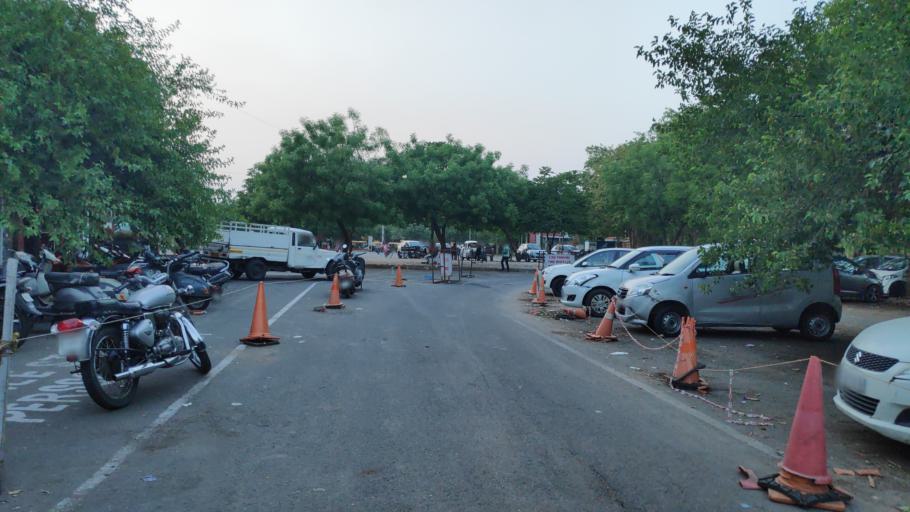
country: IN
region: Punjab
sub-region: Ajitgarh
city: Mohali
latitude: 30.7172
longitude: 76.7443
